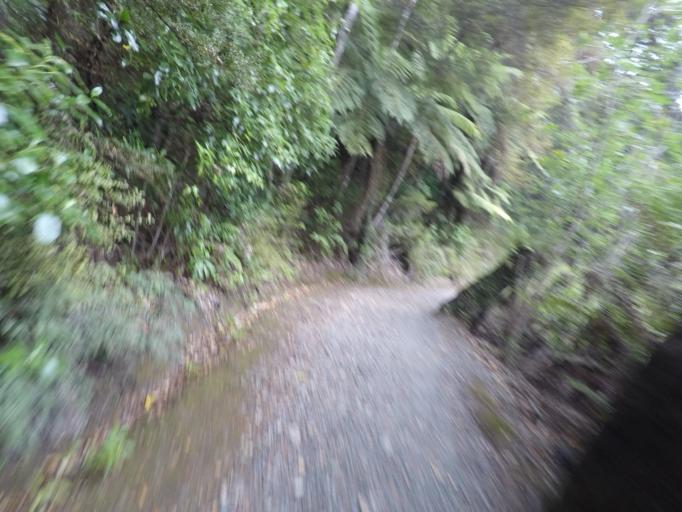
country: NZ
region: Northland
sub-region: Whangarei
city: Whangarei
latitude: -35.7130
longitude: 174.3306
